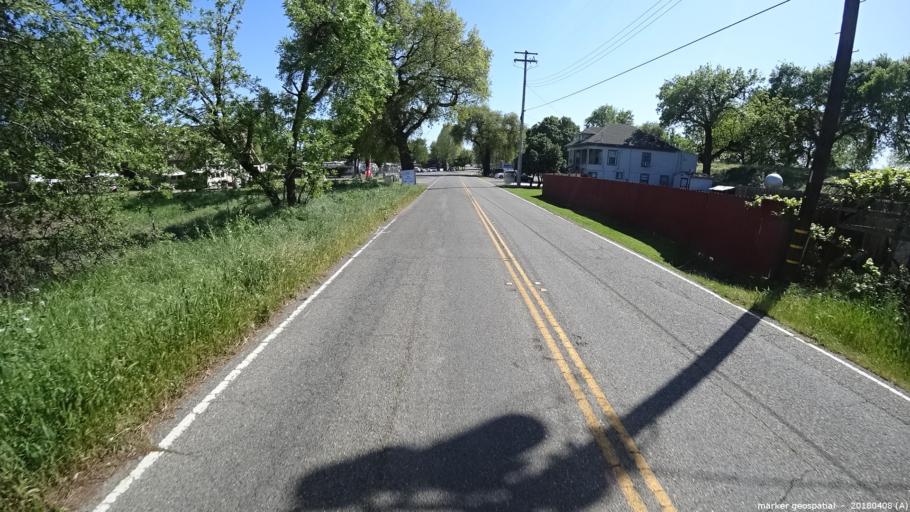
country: US
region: California
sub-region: Sacramento County
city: Parkway
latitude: 38.4594
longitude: -121.5013
